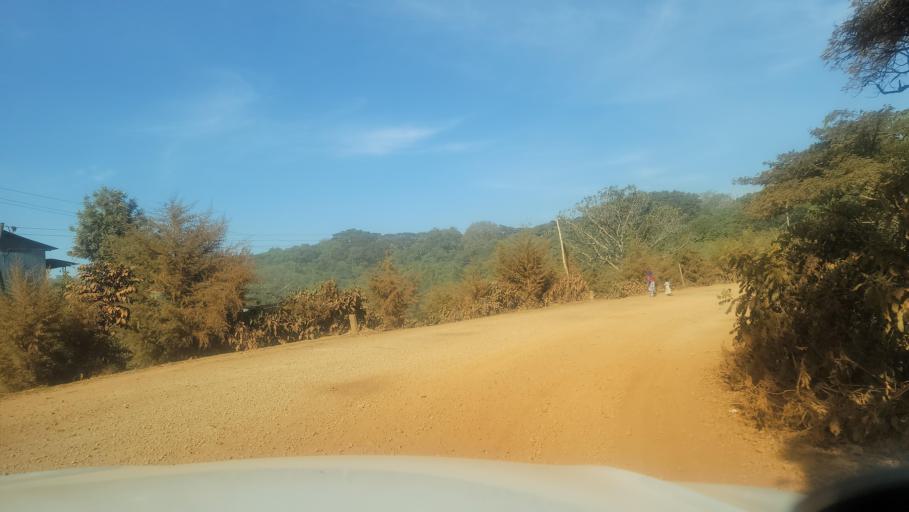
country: ET
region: Oromiya
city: Agaro
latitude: 7.8371
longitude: 36.5532
